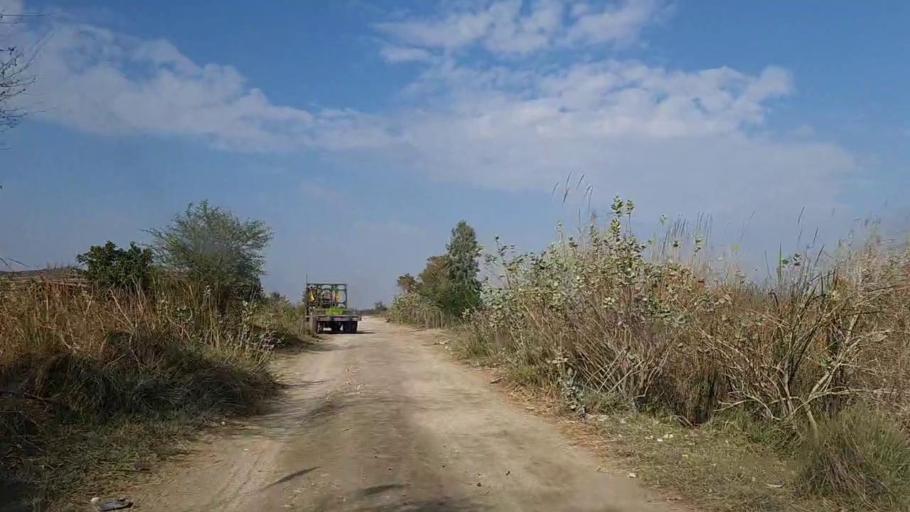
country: PK
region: Sindh
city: Sanghar
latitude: 26.2692
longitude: 69.0121
